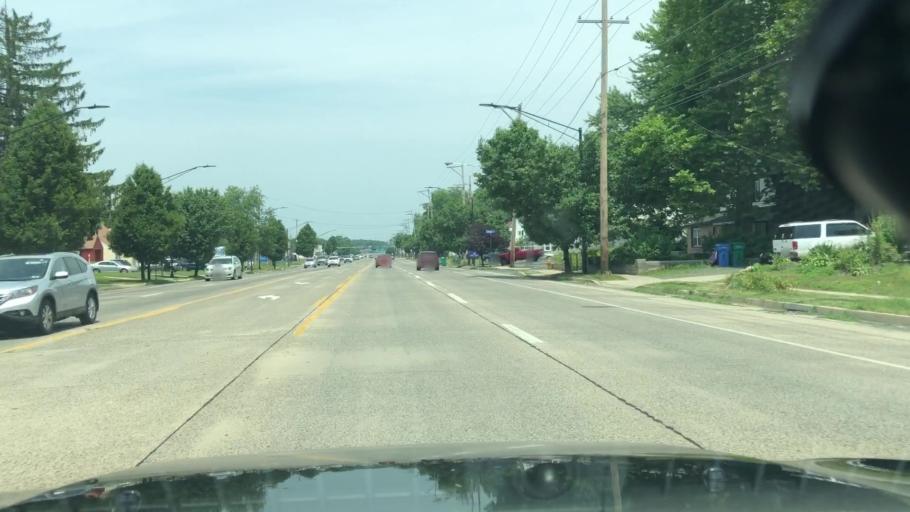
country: US
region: Pennsylvania
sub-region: Bucks County
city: Bristol
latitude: 40.1036
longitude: -74.8753
